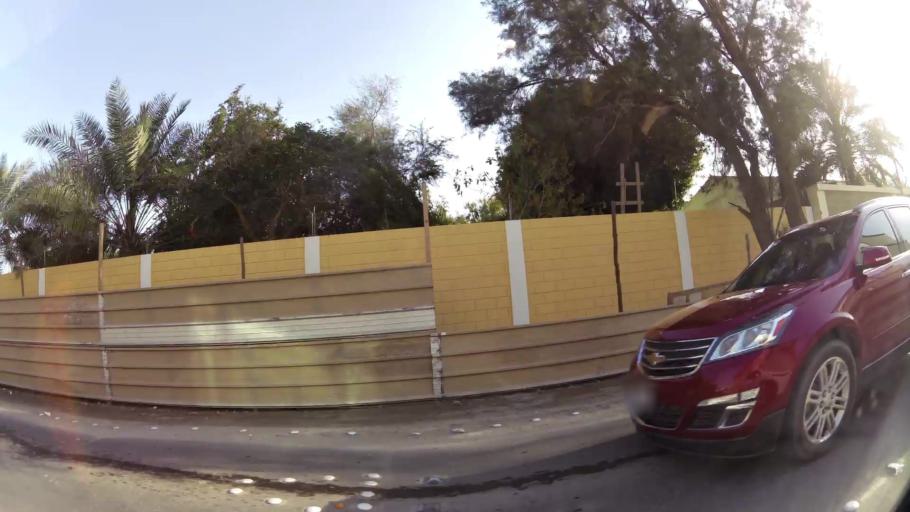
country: BH
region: Manama
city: Jidd Hafs
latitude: 26.2033
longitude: 50.4940
